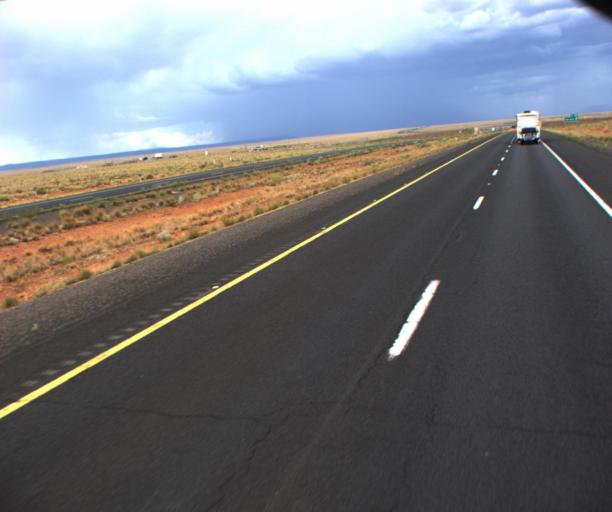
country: US
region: Arizona
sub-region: Coconino County
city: LeChee
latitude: 35.1164
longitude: -111.0822
